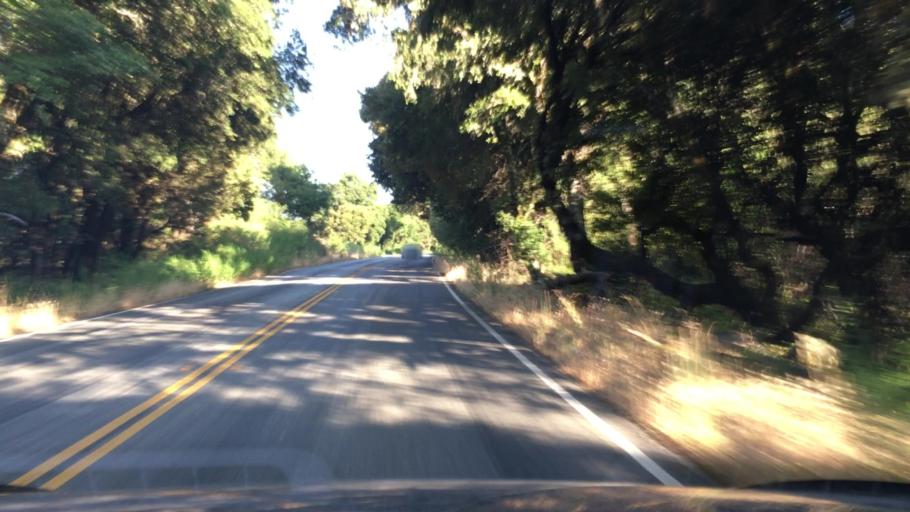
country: US
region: California
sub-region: San Mateo County
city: Portola Valley
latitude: 37.3229
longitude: -122.2007
